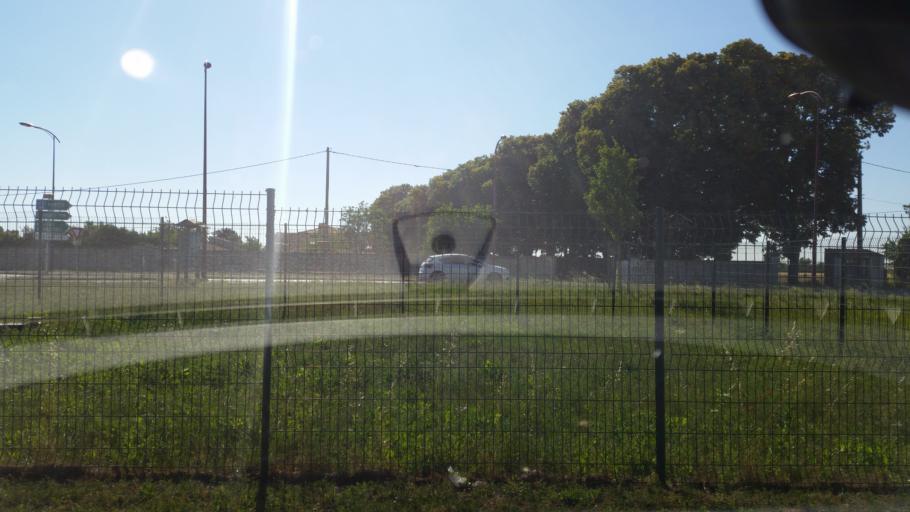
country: FR
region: Poitou-Charentes
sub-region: Departement de la Charente-Maritime
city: Marans
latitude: 46.2960
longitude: -0.9907
